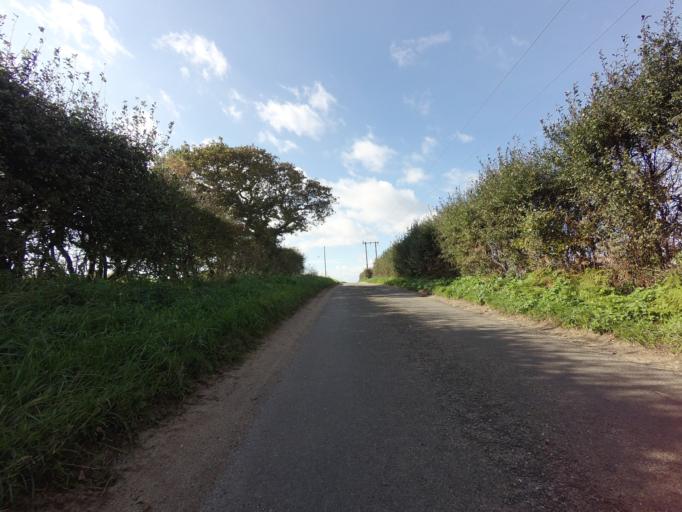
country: GB
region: England
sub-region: Norfolk
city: Hunstanton
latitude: 52.9362
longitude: 0.6229
